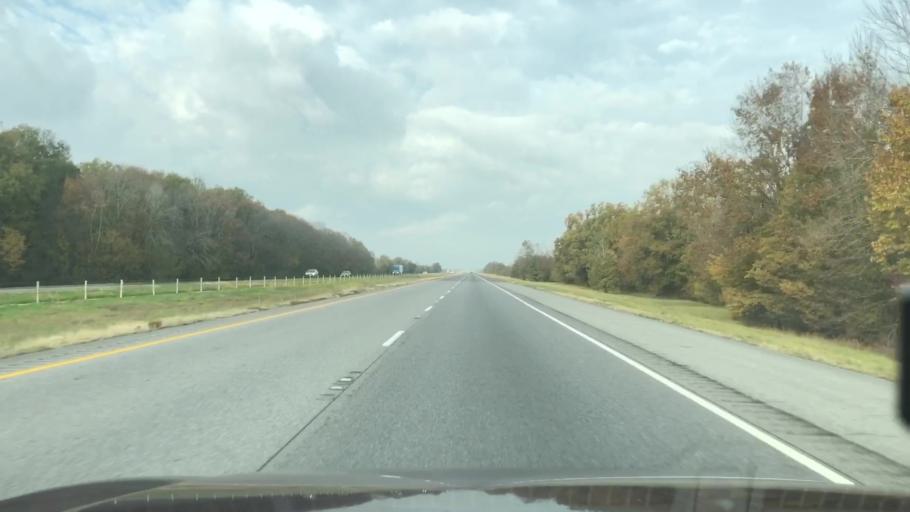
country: US
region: Louisiana
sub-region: Richland Parish
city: Delhi
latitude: 32.4266
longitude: -91.3864
